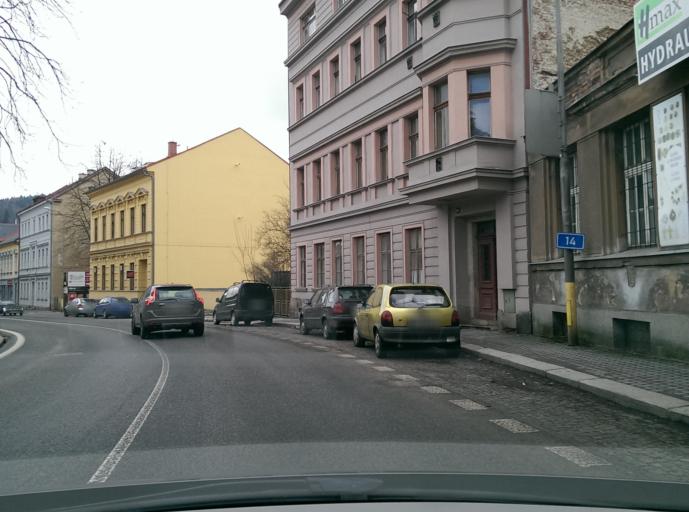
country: CZ
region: Liberecky
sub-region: Okres Jablonec nad Nisou
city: Jablonec nad Nisou
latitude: 50.7242
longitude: 15.1811
